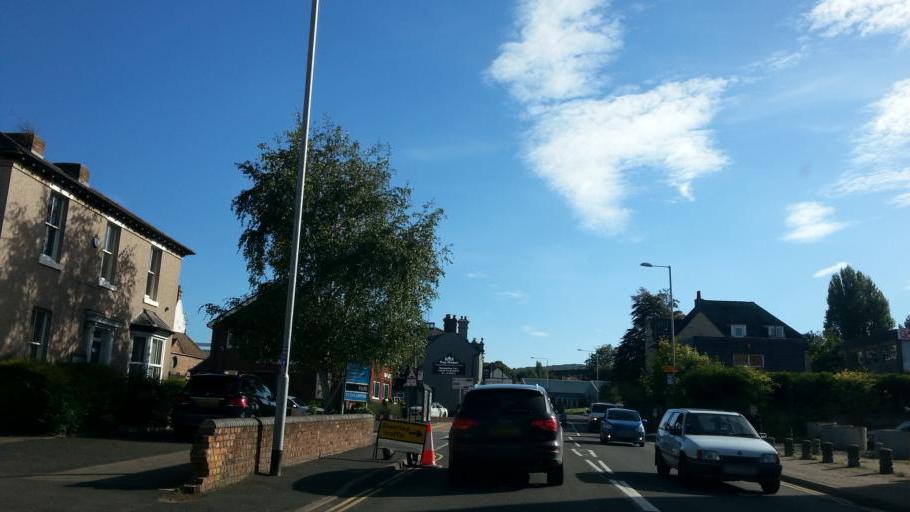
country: GB
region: England
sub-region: Telford and Wrekin
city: Wellington
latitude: 52.7004
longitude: -2.5211
